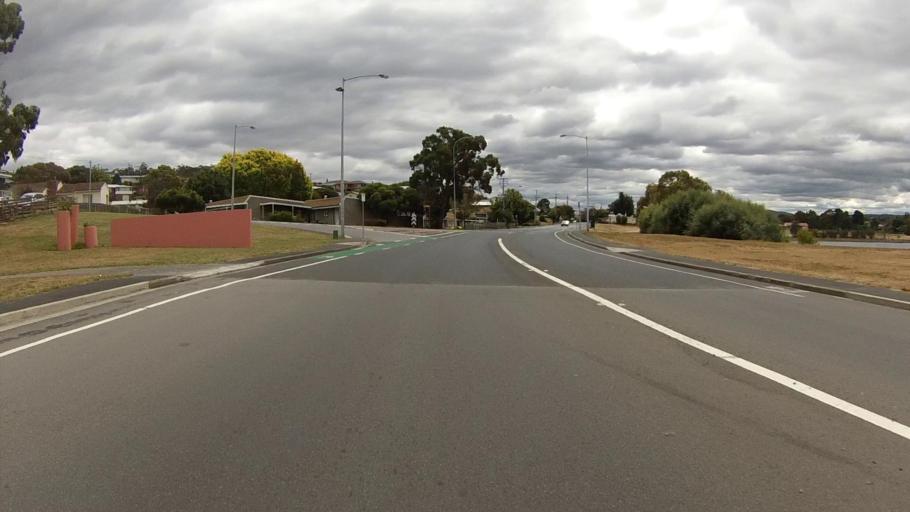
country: AU
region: Tasmania
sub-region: Glenorchy
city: Claremont
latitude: -42.7867
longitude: 147.2517
